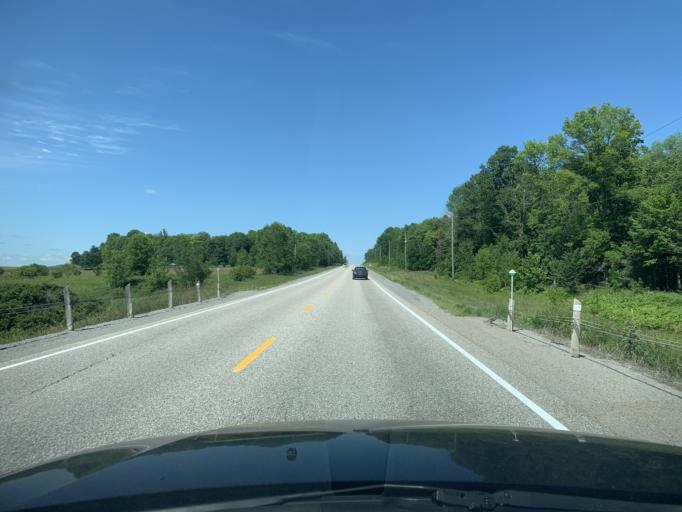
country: CA
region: Ontario
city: Renfrew
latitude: 45.5175
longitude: -76.8245
